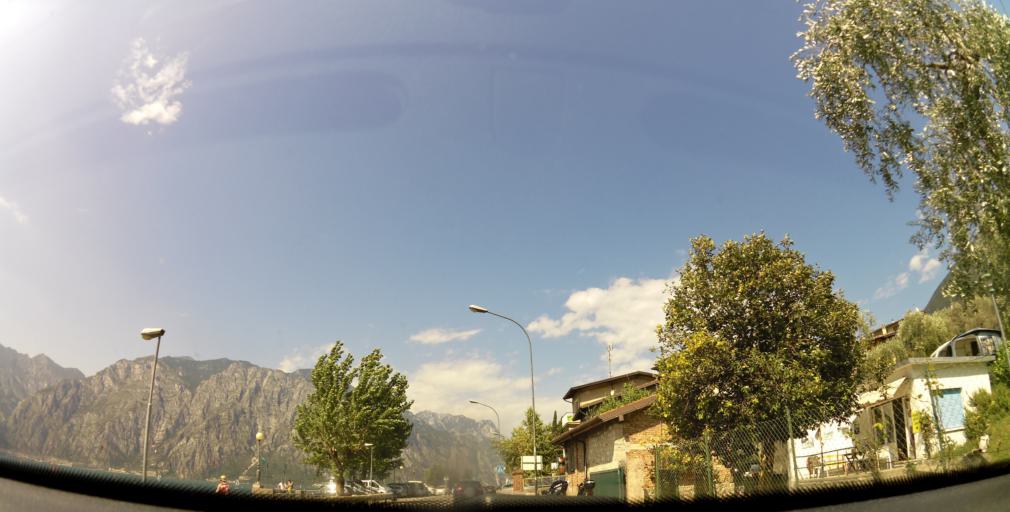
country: IT
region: Lombardy
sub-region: Provincia di Brescia
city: Limone sul Garda
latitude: 45.7990
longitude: 10.8375
